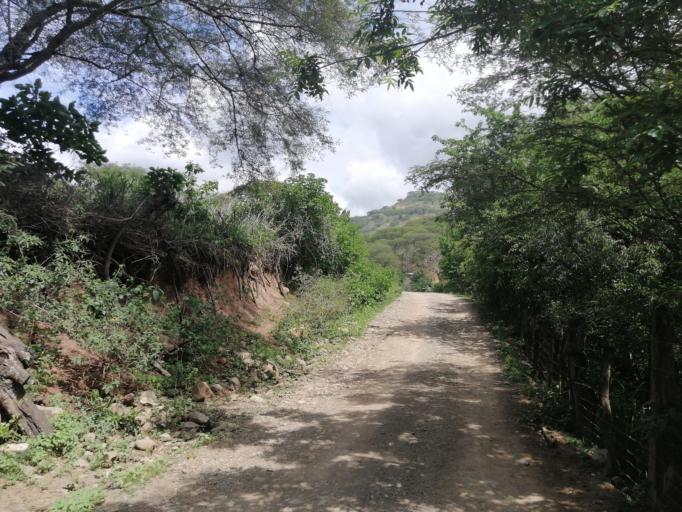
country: EC
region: Loja
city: Catacocha
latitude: -4.0146
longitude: -79.6812
